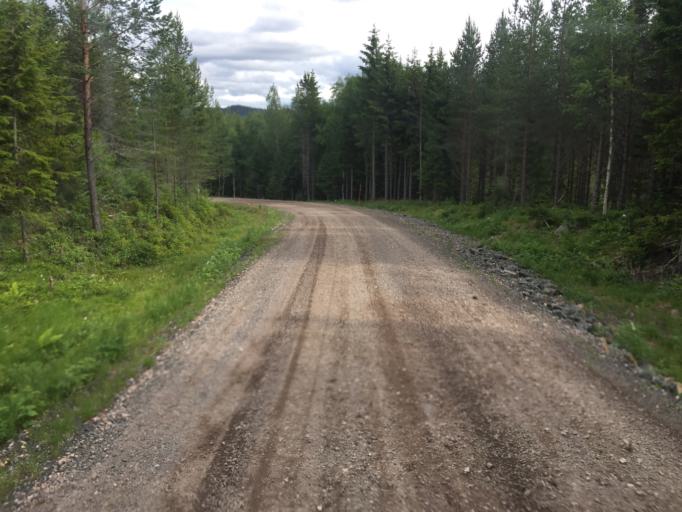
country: SE
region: Dalarna
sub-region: Malung-Saelens kommun
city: Malung
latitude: 60.8748
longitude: 13.6284
